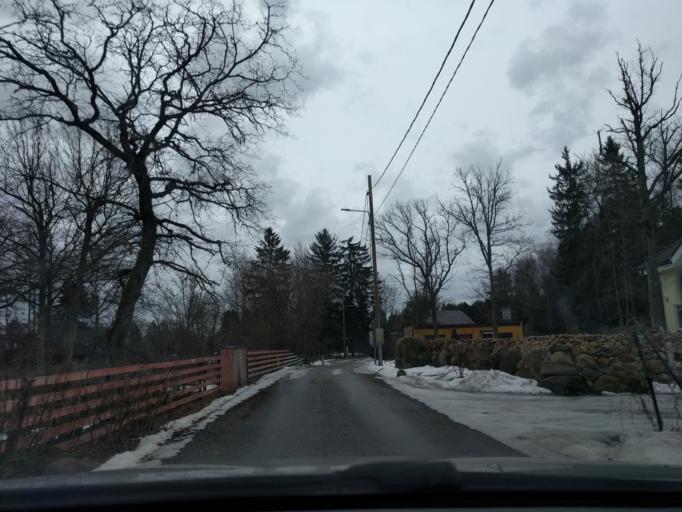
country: EE
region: Harju
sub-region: Viimsi vald
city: Viimsi
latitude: 59.5165
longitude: 24.9059
